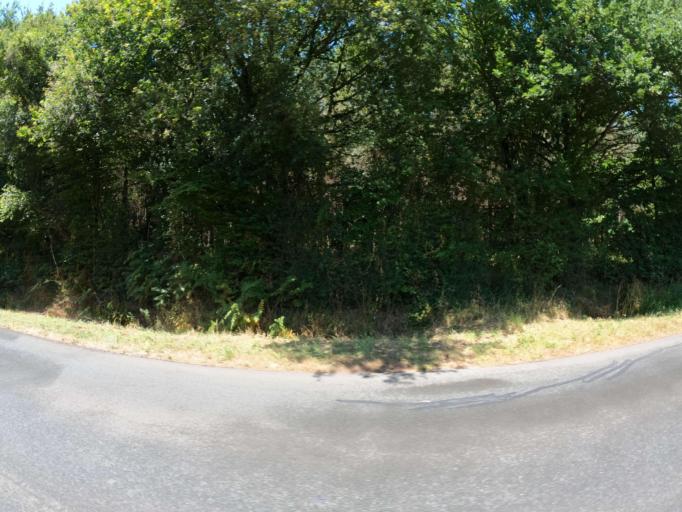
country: FR
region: Pays de la Loire
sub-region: Departement de Maine-et-Loire
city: Champigne
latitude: 47.6343
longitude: -0.5800
